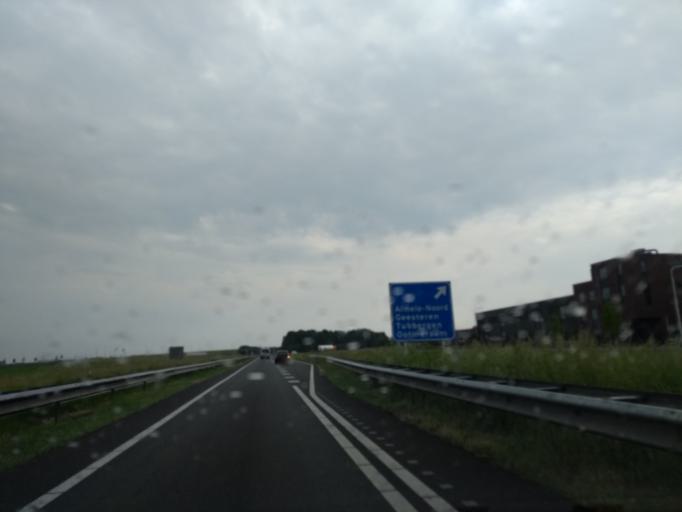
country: NL
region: Overijssel
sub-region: Gemeente Twenterand
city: Vriezenveen
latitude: 52.4080
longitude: 6.6377
